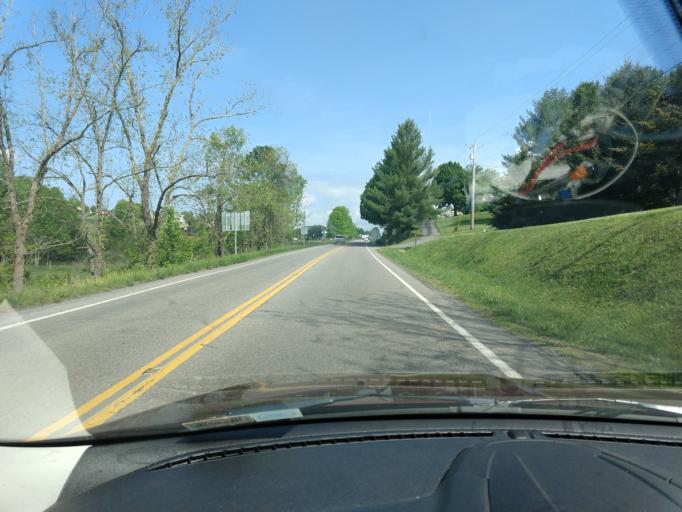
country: US
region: Virginia
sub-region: Russell County
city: Honaker
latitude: 36.9611
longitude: -81.9331
